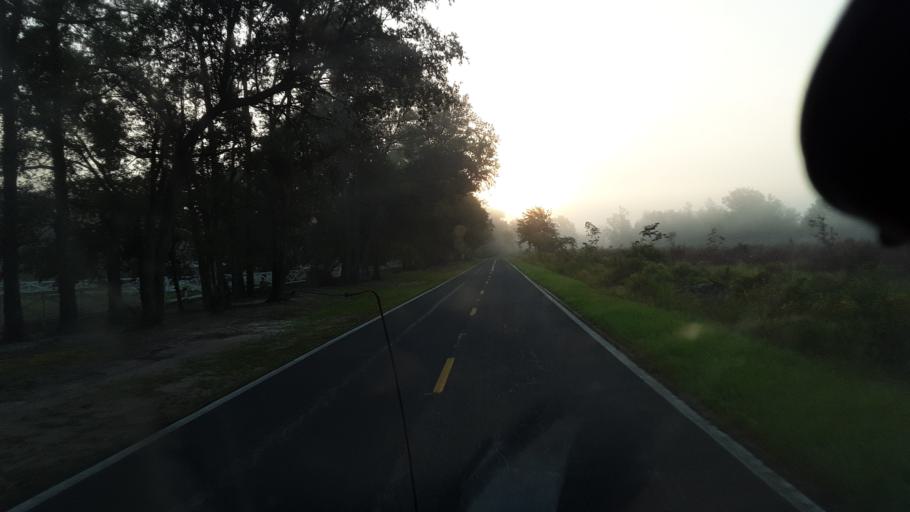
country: US
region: South Carolina
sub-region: Clarendon County
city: Manning
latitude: 33.7304
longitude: -80.0980
